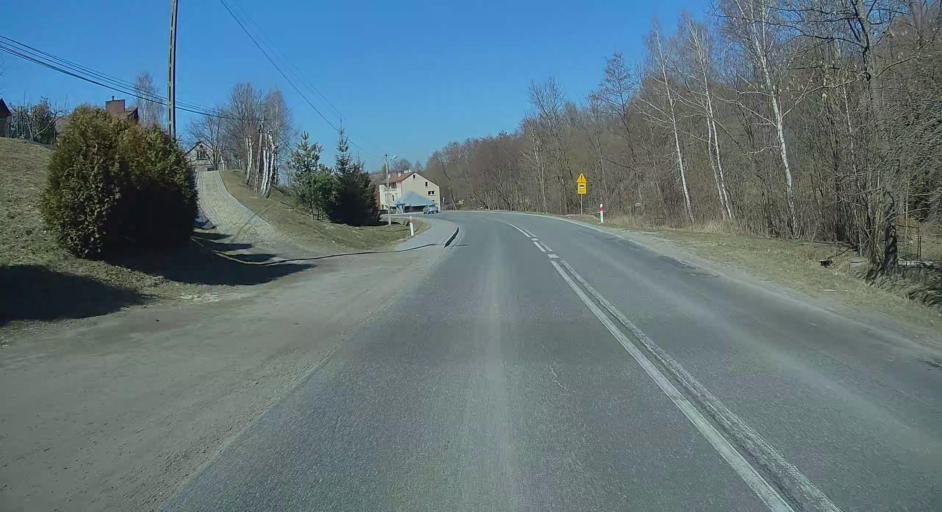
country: PL
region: Subcarpathian Voivodeship
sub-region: Powiat rzeszowski
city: Hyzne
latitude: 49.9039
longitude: 22.2089
